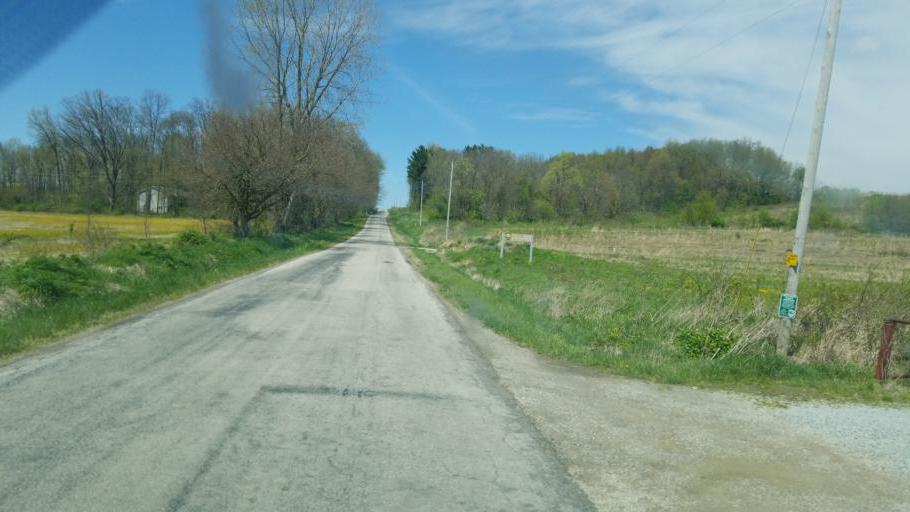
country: US
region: Ohio
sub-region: Wayne County
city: Shreve
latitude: 40.7687
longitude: -82.1173
